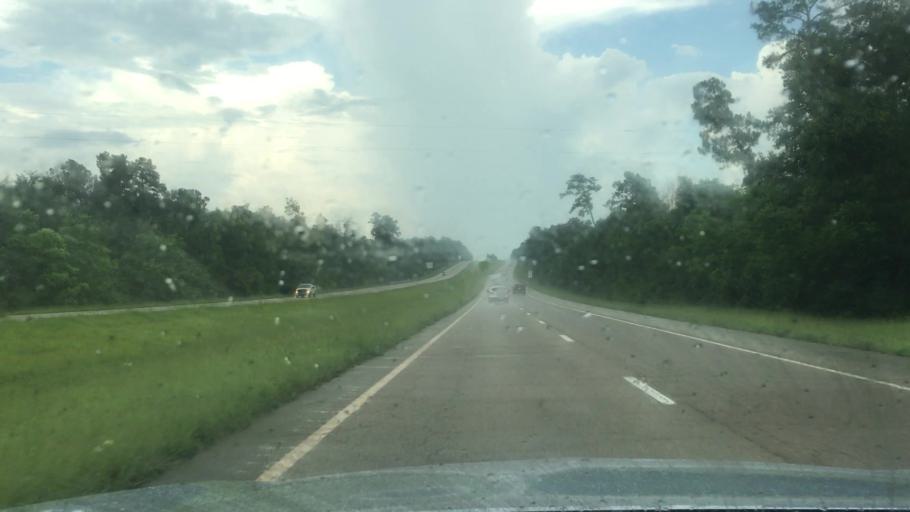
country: US
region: Mississippi
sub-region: Lamar County
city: Purvis
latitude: 31.1465
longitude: -89.3648
